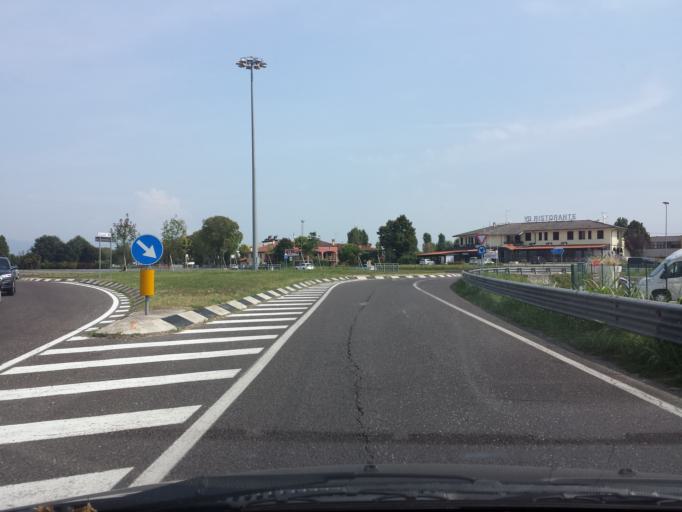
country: IT
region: Veneto
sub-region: Provincia di Vicenza
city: Monticello Conte Otto
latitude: 45.6106
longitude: 11.5624
